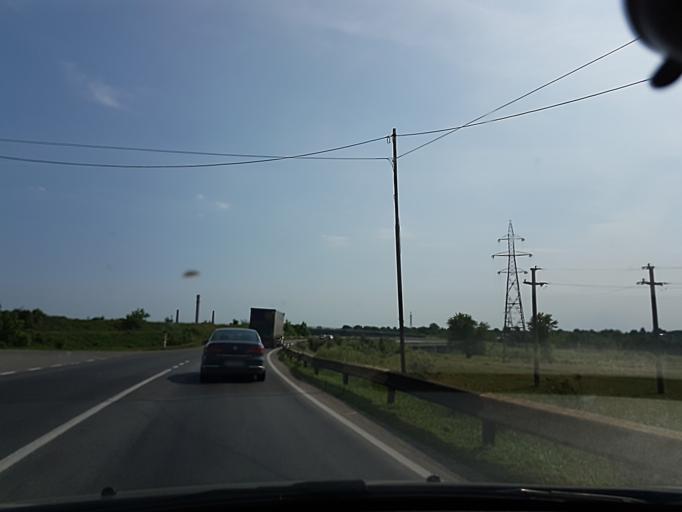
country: RO
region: Prahova
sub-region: Comuna Blejoiu
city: Blejoi
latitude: 44.9986
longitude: 26.0183
